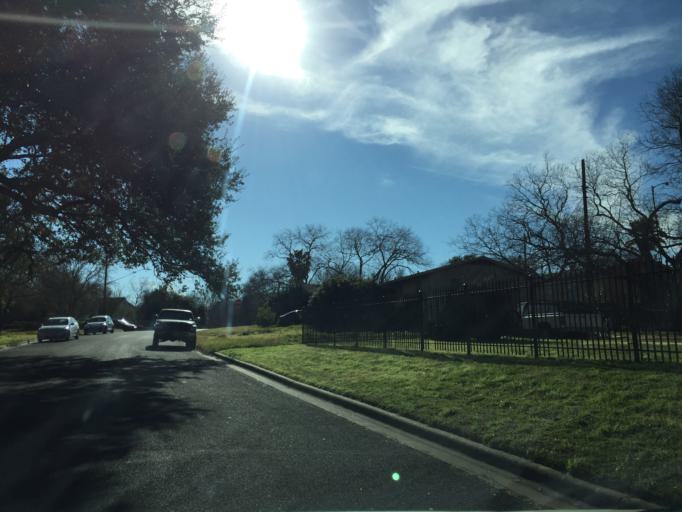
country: US
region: Texas
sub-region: Travis County
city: Austin
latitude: 30.2358
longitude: -97.7510
